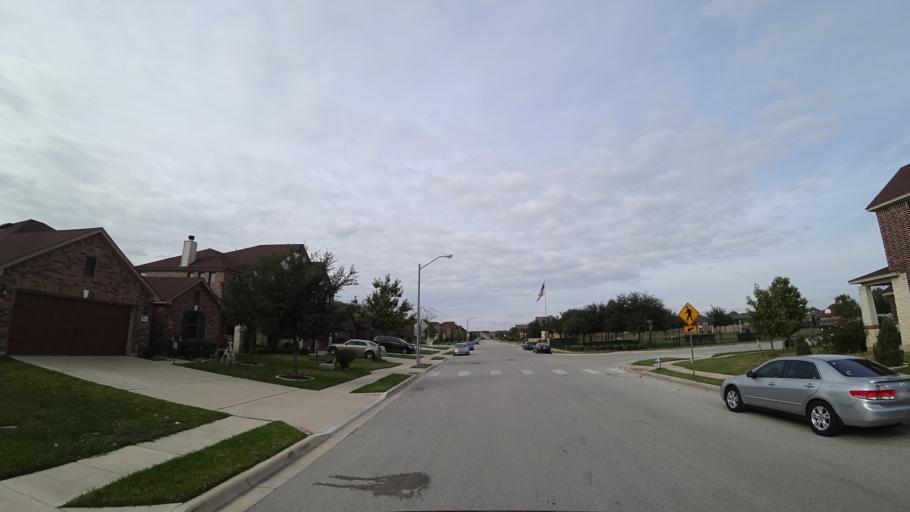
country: US
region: Texas
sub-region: Travis County
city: Wells Branch
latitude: 30.4281
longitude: -97.6623
